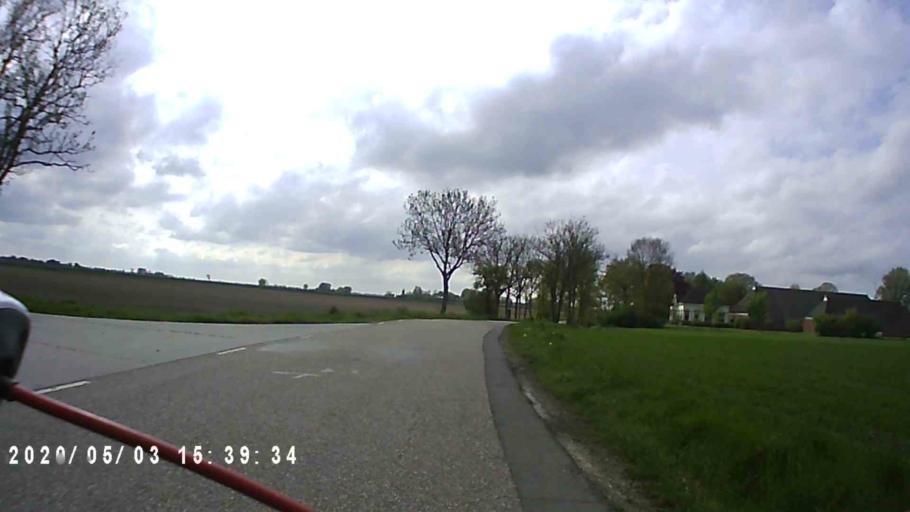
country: NL
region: Groningen
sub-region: Gemeente Zuidhorn
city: Oldehove
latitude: 53.3302
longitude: 6.4390
